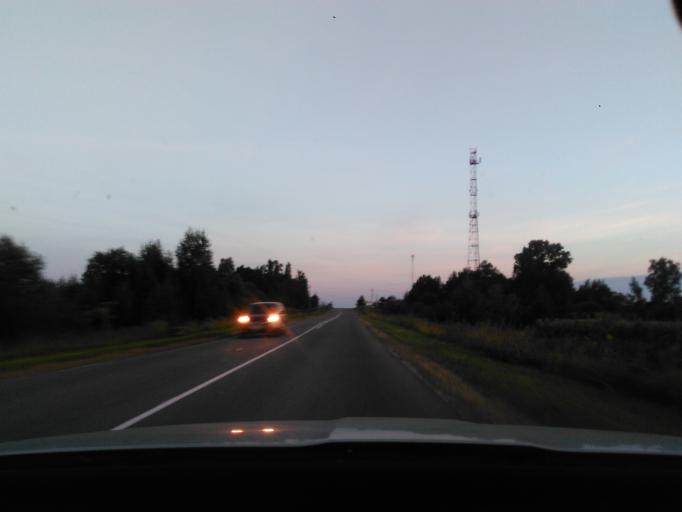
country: RU
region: Moskovskaya
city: Klin
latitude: 56.2348
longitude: 36.7504
